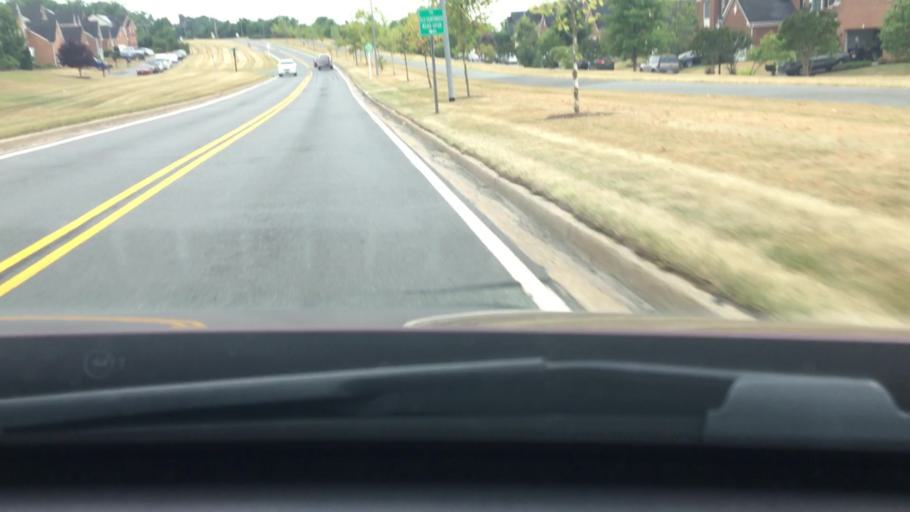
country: US
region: Maryland
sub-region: Prince George's County
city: Calverton
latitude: 39.0684
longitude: -76.9212
